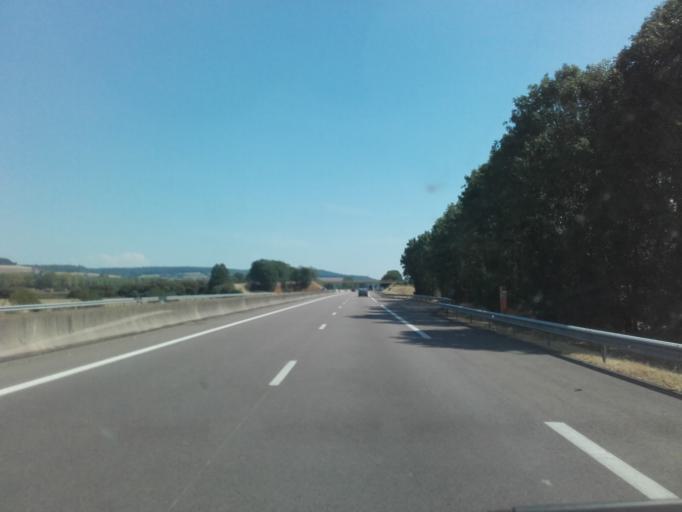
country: FR
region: Bourgogne
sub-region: Departement de la Cote-d'Or
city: Vitteaux
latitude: 47.3274
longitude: 4.4840
